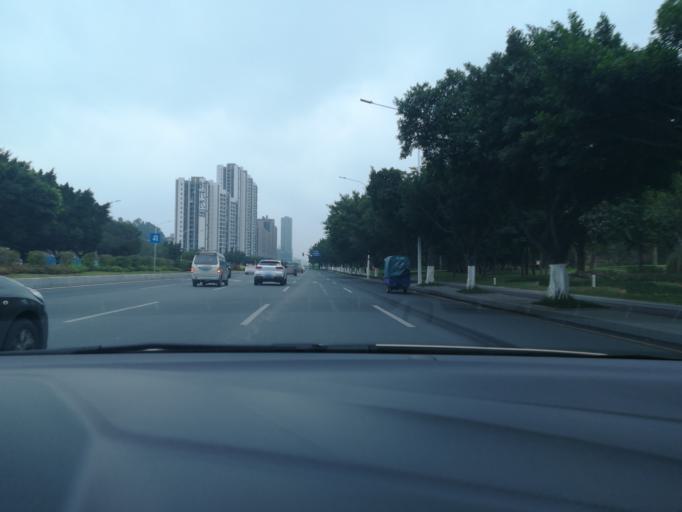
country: CN
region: Guangdong
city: Nansha
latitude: 22.8006
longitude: 113.5601
